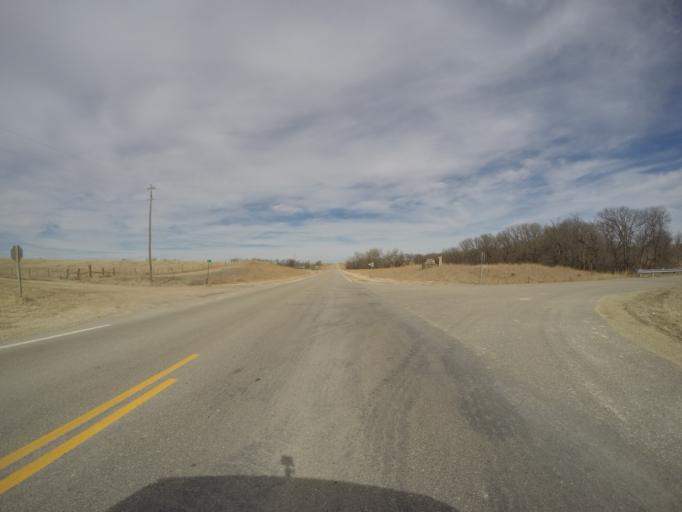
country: US
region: Nebraska
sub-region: Nuckolls County
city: Superior
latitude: 39.9148
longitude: -98.1180
